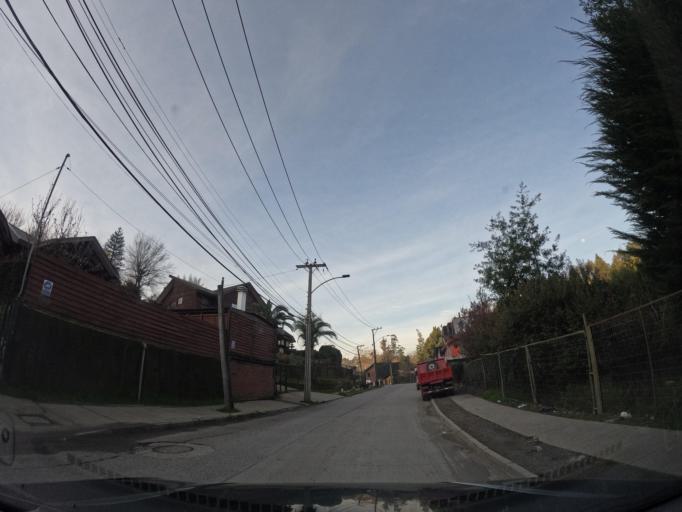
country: CL
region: Biobio
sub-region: Provincia de Concepcion
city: Concepcion
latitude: -36.8409
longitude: -73.0082
